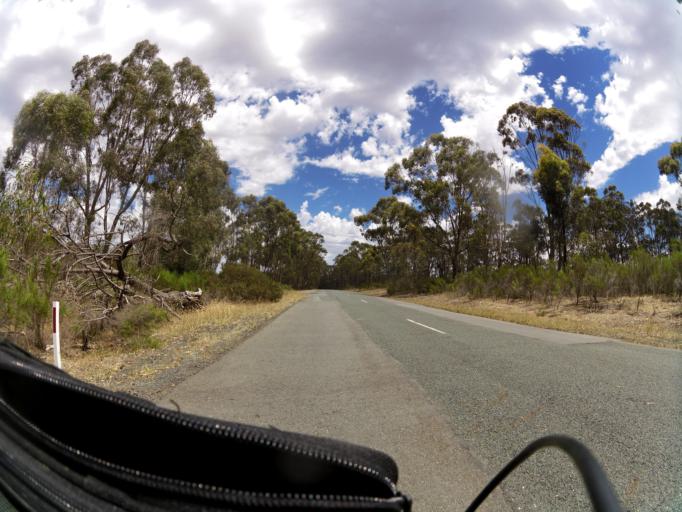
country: AU
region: Victoria
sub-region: Greater Shepparton
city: Shepparton
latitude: -36.6844
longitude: 145.1844
